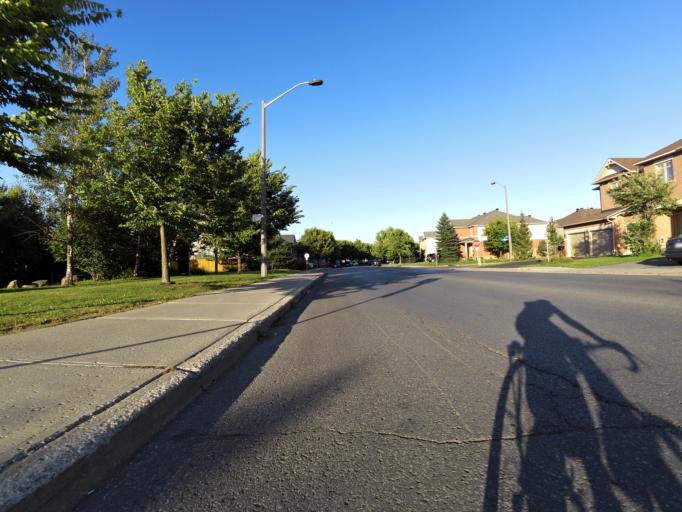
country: CA
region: Ontario
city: Bells Corners
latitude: 45.2799
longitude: -75.7376
